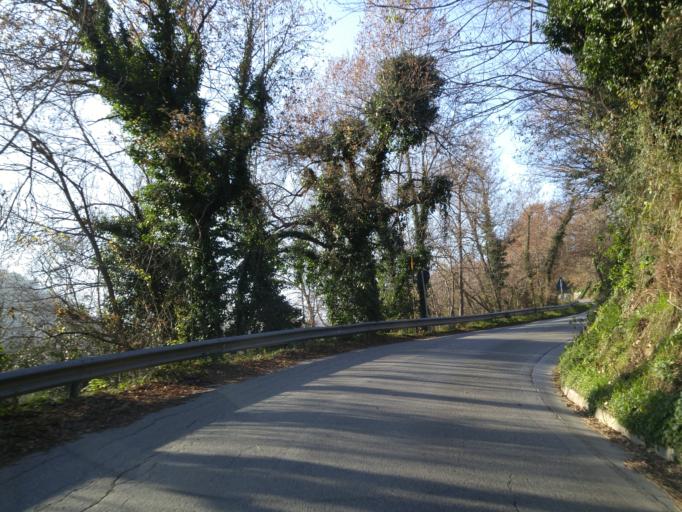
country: IT
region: The Marches
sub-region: Provincia di Pesaro e Urbino
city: Isola del Piano
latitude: 43.7548
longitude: 12.8035
